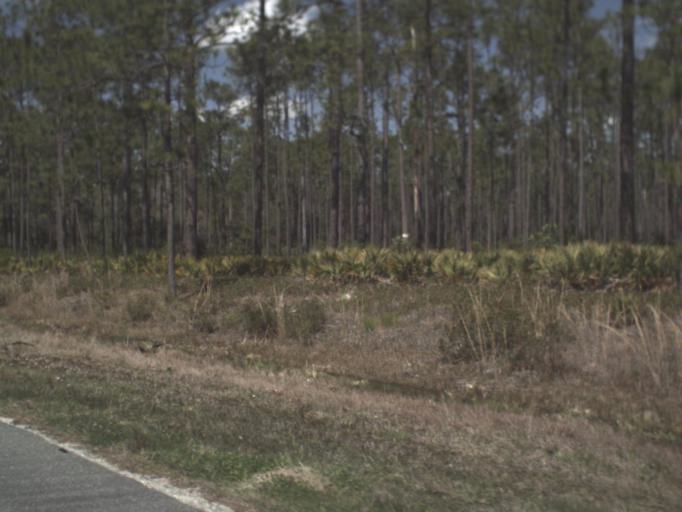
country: US
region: Florida
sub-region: Gadsden County
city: Midway
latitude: 30.3417
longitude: -84.4938
